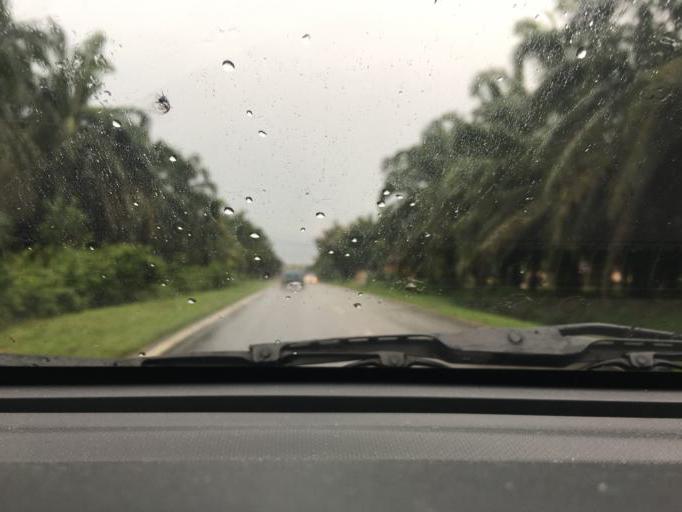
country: MY
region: Kedah
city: Sungai Petani
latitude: 5.6469
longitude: 100.6322
